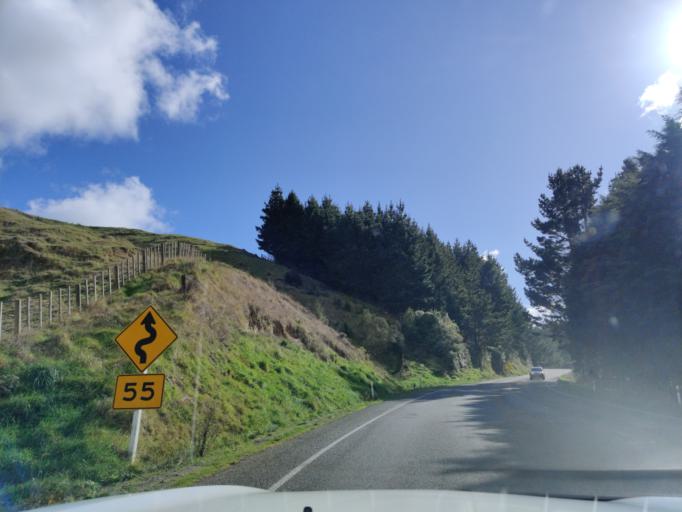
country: NZ
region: Manawatu-Wanganui
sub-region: Palmerston North City
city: Palmerston North
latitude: -40.2975
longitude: 175.8093
